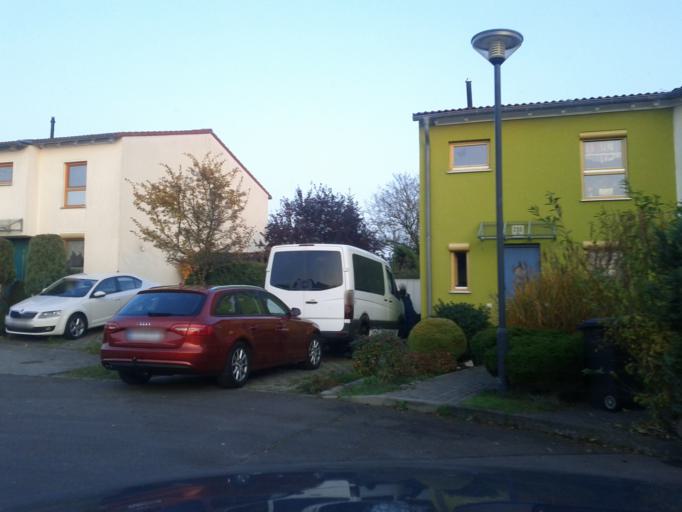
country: DE
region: Berlin
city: Mahlsdorf
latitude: 52.4982
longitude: 13.6239
